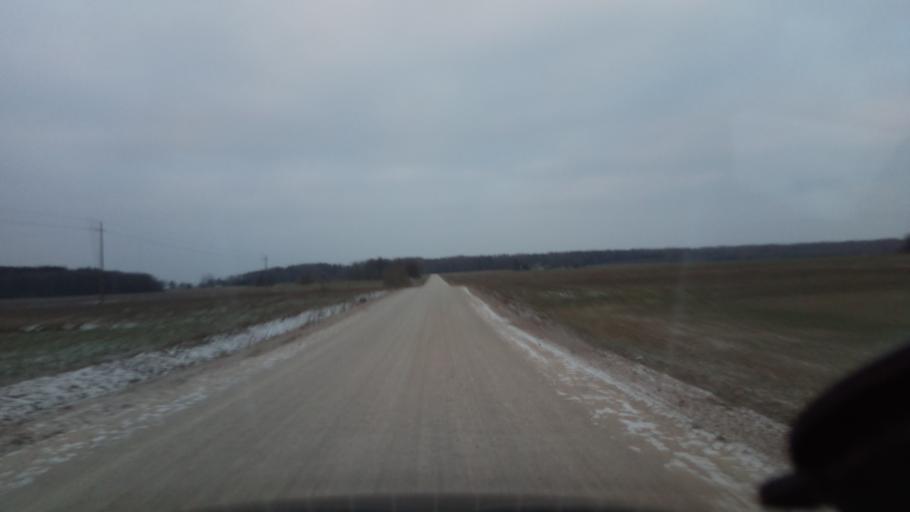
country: LT
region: Alytaus apskritis
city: Varena
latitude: 54.1170
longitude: 24.7412
